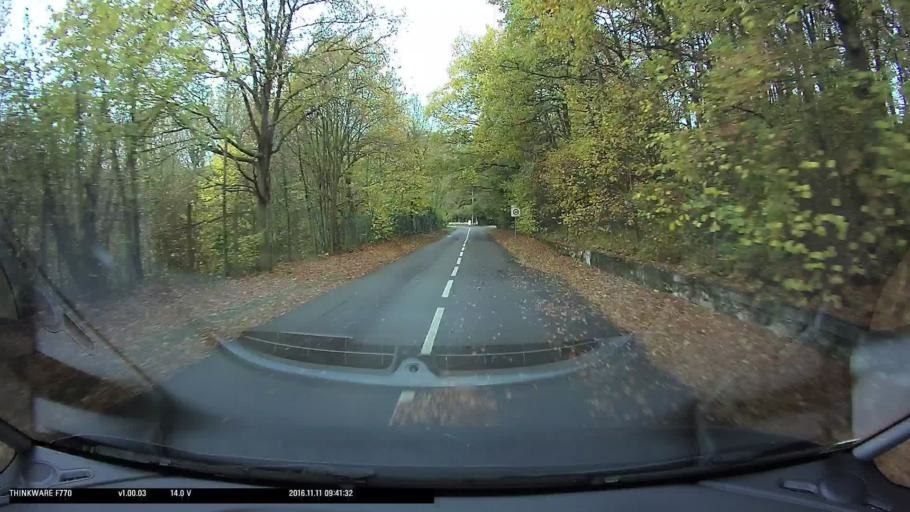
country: FR
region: Ile-de-France
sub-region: Departement du Val-d'Oise
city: Osny
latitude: 49.0680
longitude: 2.0593
